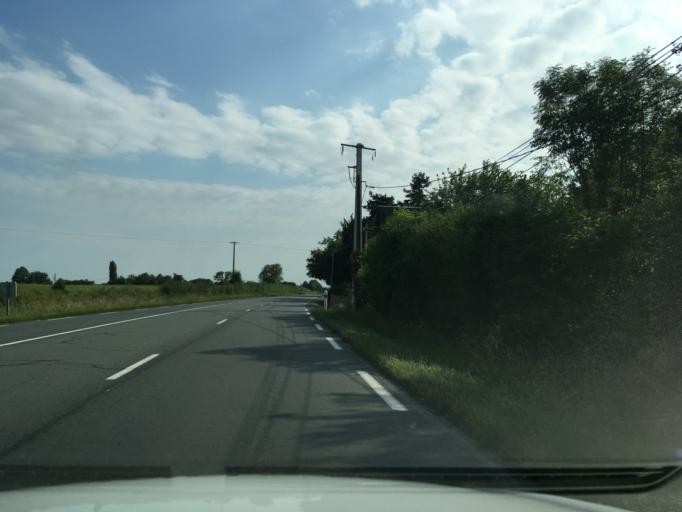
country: FR
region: Poitou-Charentes
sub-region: Departement des Deux-Sevres
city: Champdeniers-Saint-Denis
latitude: 46.5030
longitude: -0.3379
